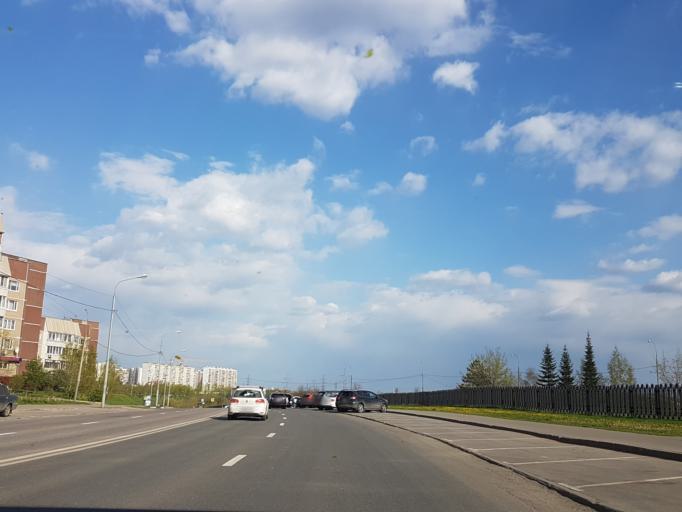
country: RU
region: Moskovskaya
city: Pavshino
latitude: 55.8396
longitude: 37.3600
